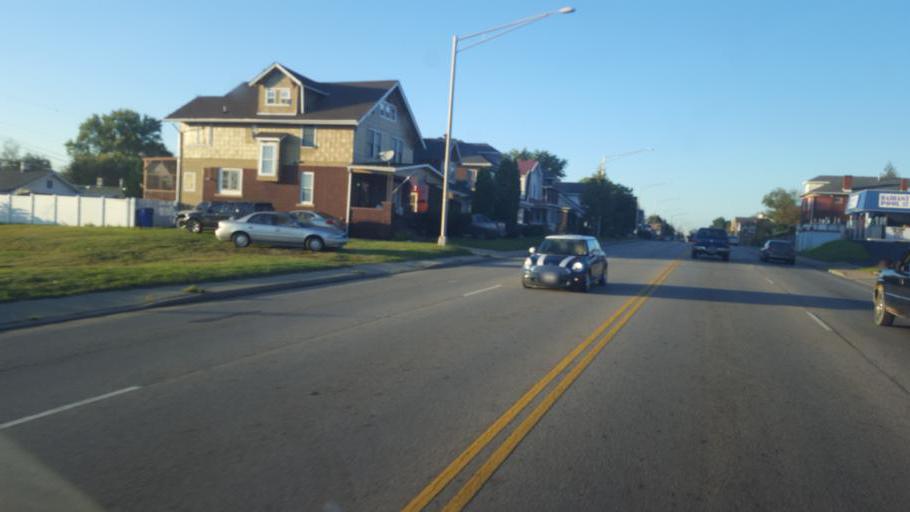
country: US
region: Ohio
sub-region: Scioto County
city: Portsmouth
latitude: 38.7493
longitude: -82.9920
